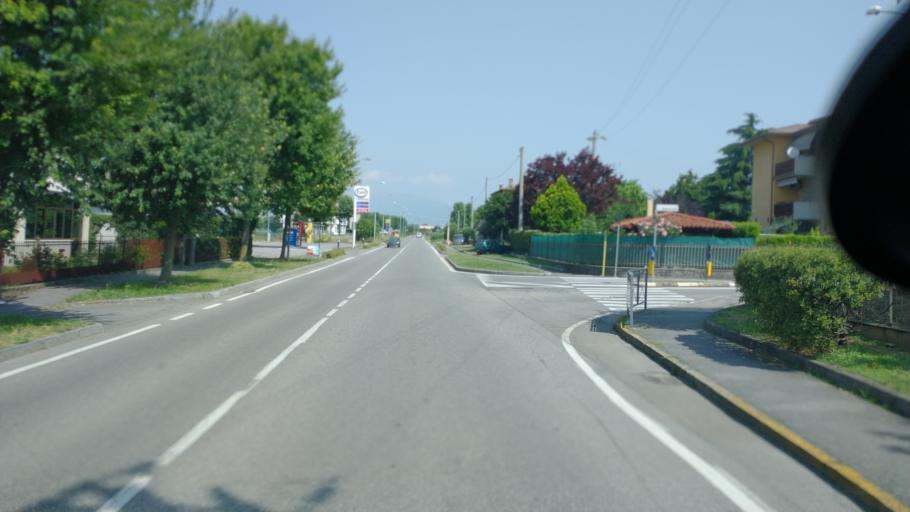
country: IT
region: Lombardy
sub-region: Provincia di Bergamo
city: Levate
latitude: 45.6275
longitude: 9.6211
